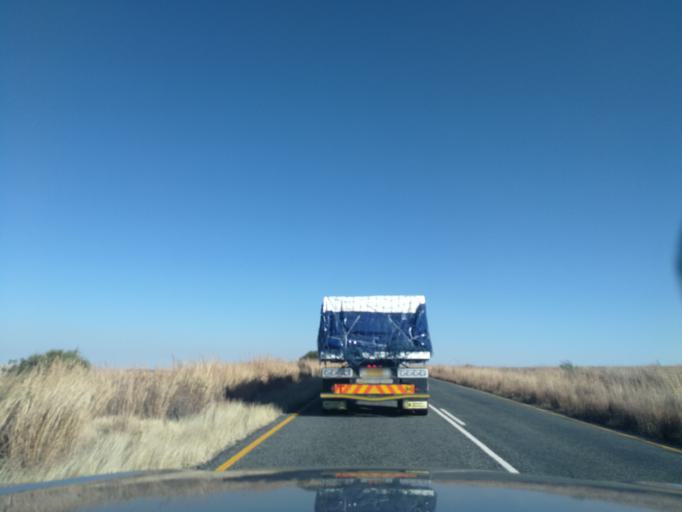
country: ZA
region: Orange Free State
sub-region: Thabo Mofutsanyana District Municipality
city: Senekal
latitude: -27.9521
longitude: 27.6034
